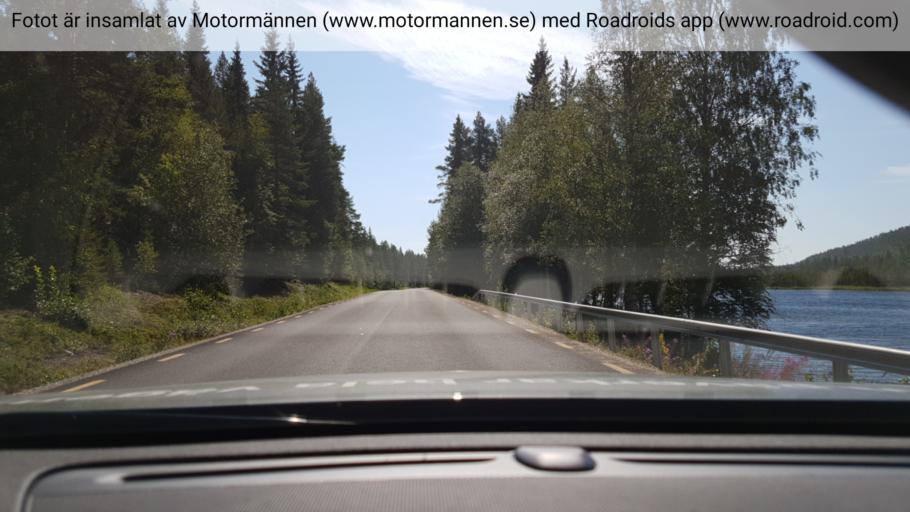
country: SE
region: Vaesterbotten
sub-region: Vindelns Kommun
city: Vindeln
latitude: 64.4410
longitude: 19.3428
